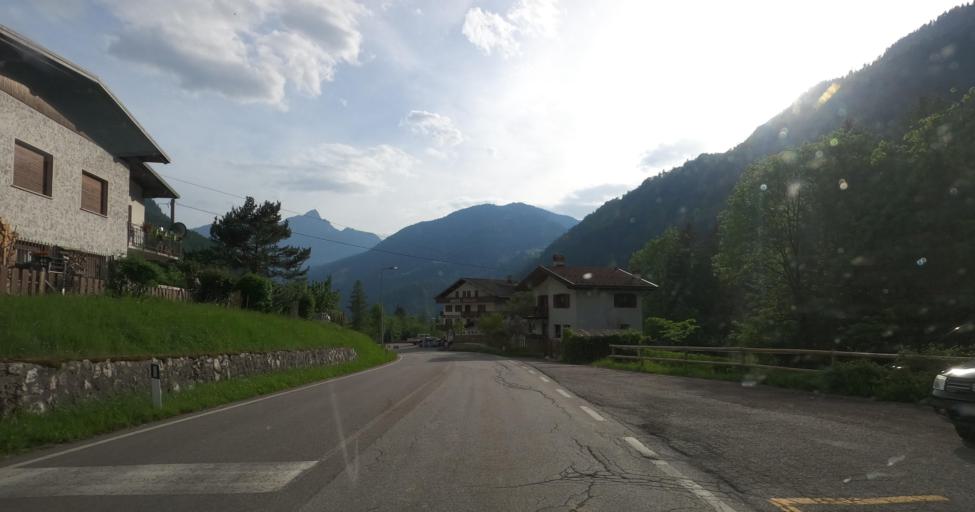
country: IT
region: Veneto
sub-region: Provincia di Belluno
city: Celat-San Tomaso Agordino
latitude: 46.3872
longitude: 11.9974
